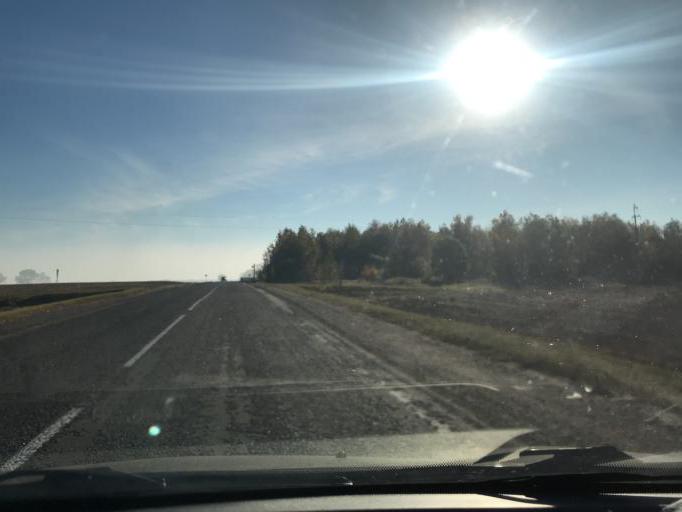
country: BY
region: Gomel
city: Brahin
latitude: 51.7845
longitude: 30.2084
